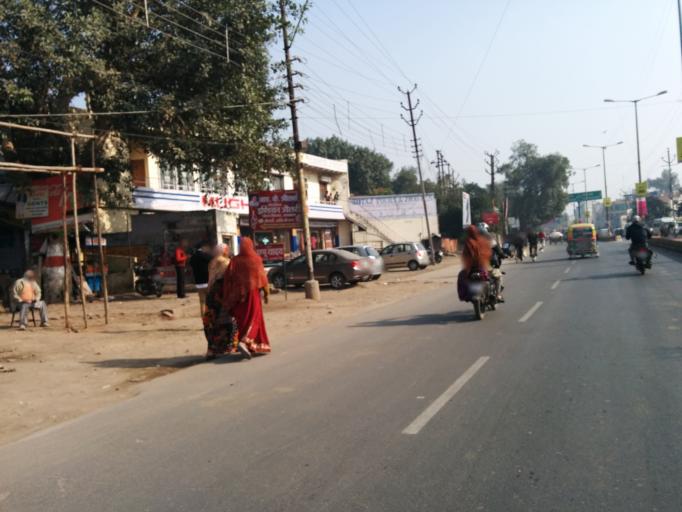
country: IN
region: Uttar Pradesh
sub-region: Agra
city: Agra
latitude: 27.1618
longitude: 78.0402
